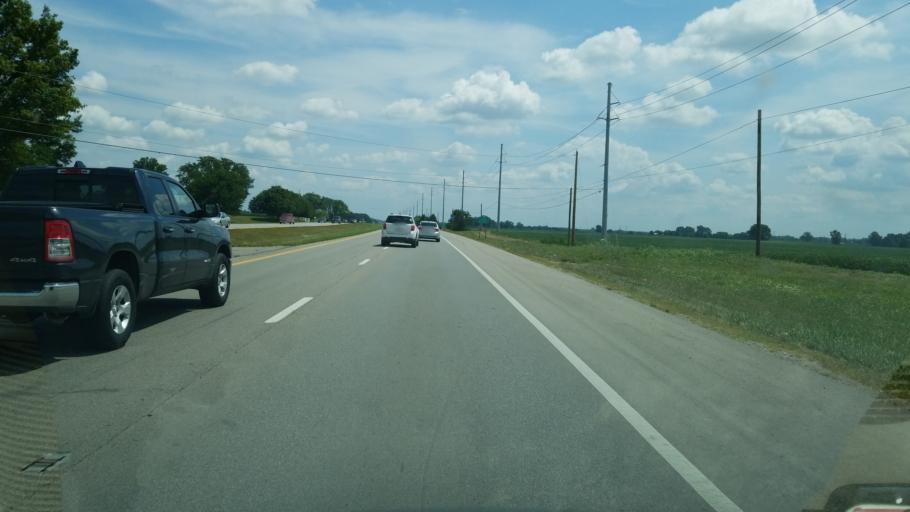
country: US
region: Ohio
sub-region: Delaware County
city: Delaware
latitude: 40.2869
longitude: -83.0120
